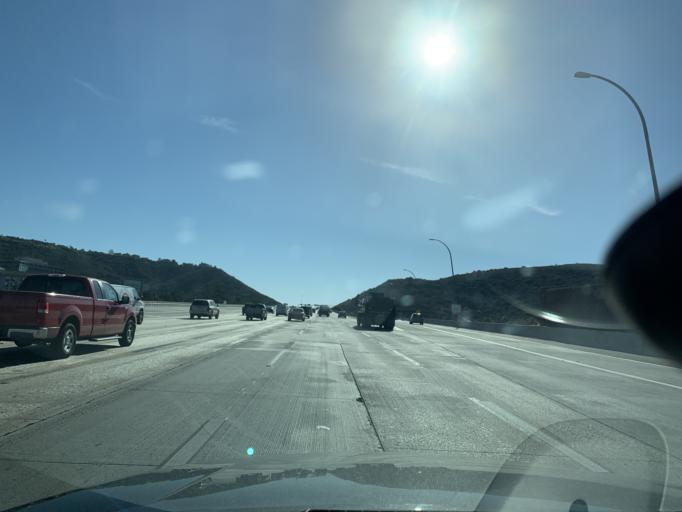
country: US
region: California
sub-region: San Diego County
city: Poway
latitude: 32.9412
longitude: -117.1106
